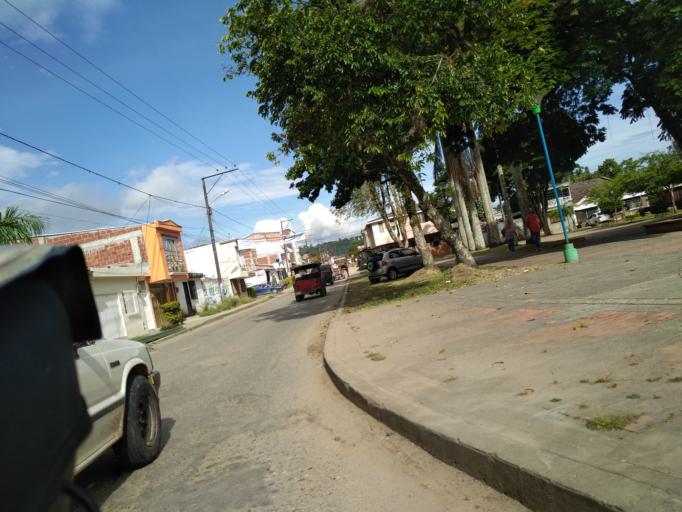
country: CO
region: Valle del Cauca
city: Caicedonia
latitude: 4.3309
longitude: -75.8240
